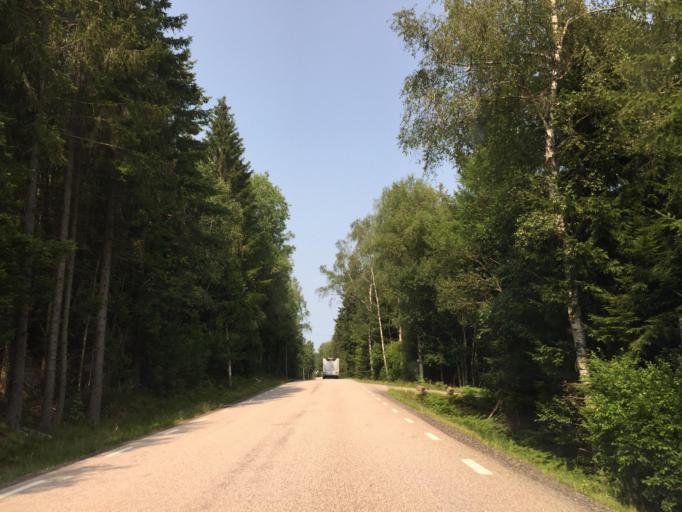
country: SE
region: Vaestra Goetaland
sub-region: Lilla Edets Kommun
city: Lilla Edet
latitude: 58.1365
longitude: 12.0092
